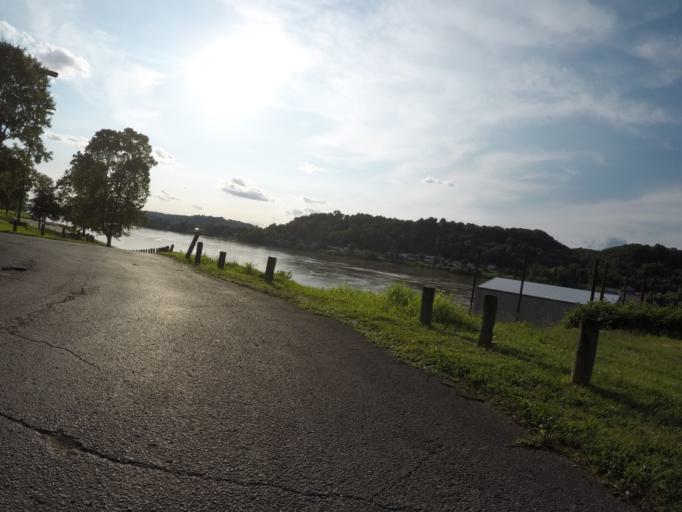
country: US
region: West Virginia
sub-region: Cabell County
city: Huntington
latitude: 38.4255
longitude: -82.4371
